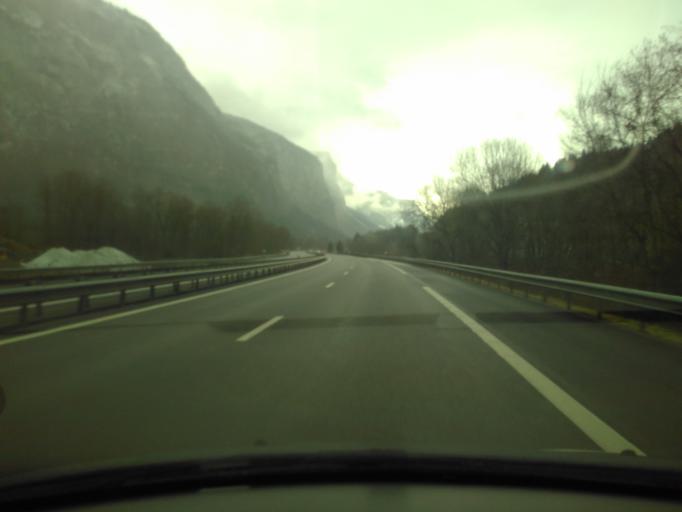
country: FR
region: Rhone-Alpes
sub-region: Departement de la Haute-Savoie
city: Magland
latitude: 46.0386
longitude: 6.6081
